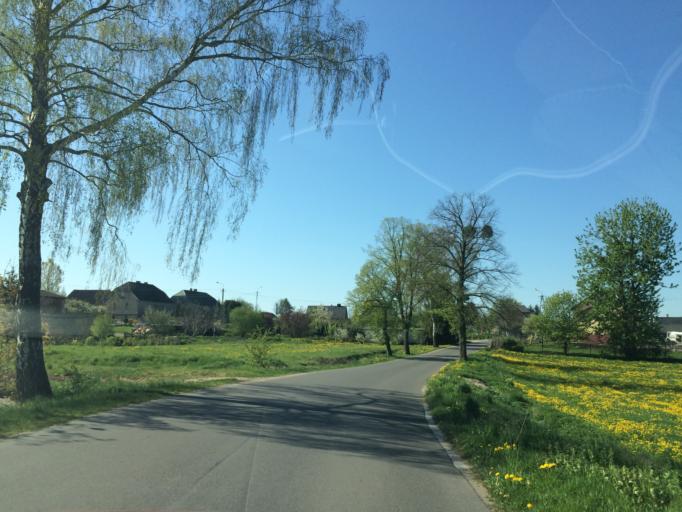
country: PL
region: Warmian-Masurian Voivodeship
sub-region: Powiat nowomiejski
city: Nowe Miasto Lubawskie
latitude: 53.4826
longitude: 19.5741
